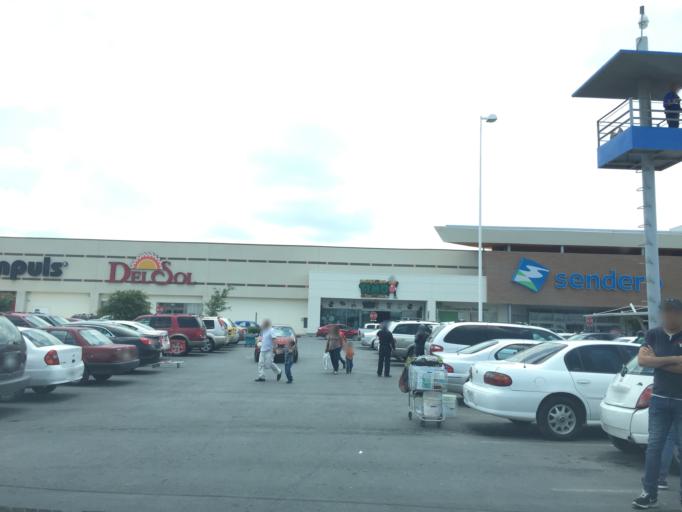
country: MX
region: Nuevo Leon
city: Apodaca
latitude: 25.7652
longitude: -100.1913
